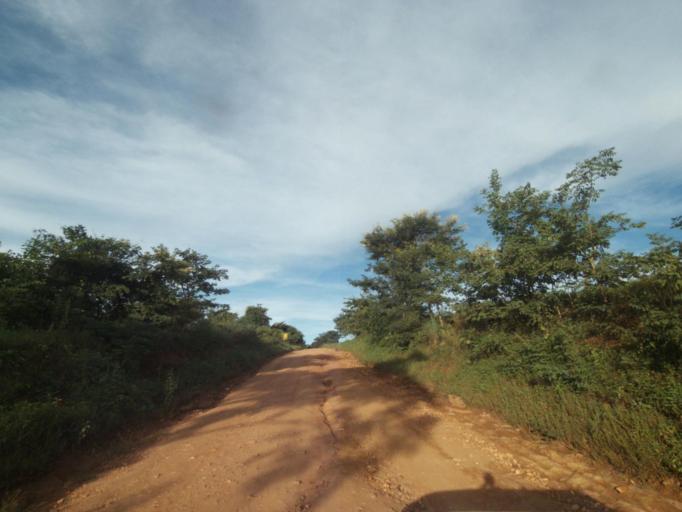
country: BR
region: Goias
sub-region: Jaragua
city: Jaragua
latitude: -15.8577
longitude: -49.3878
